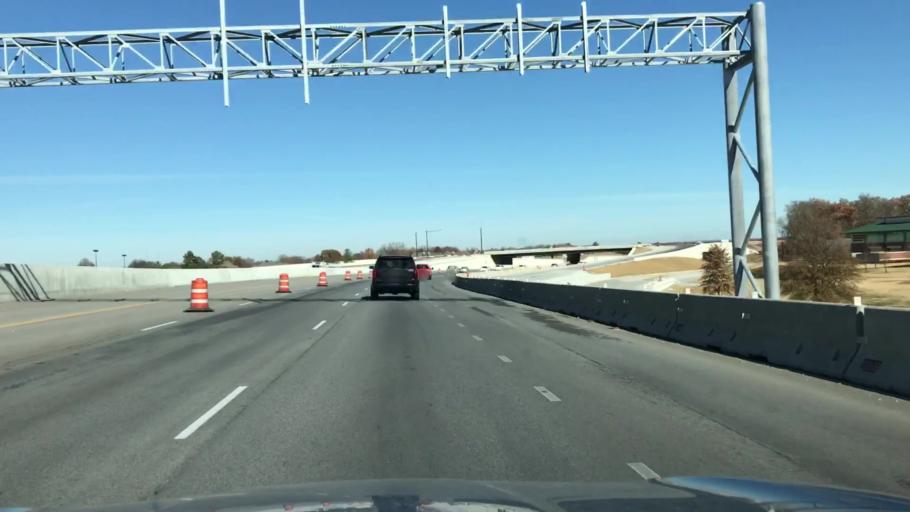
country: US
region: Arkansas
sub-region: Benton County
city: Bentonville
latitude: 36.3605
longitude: -94.1772
